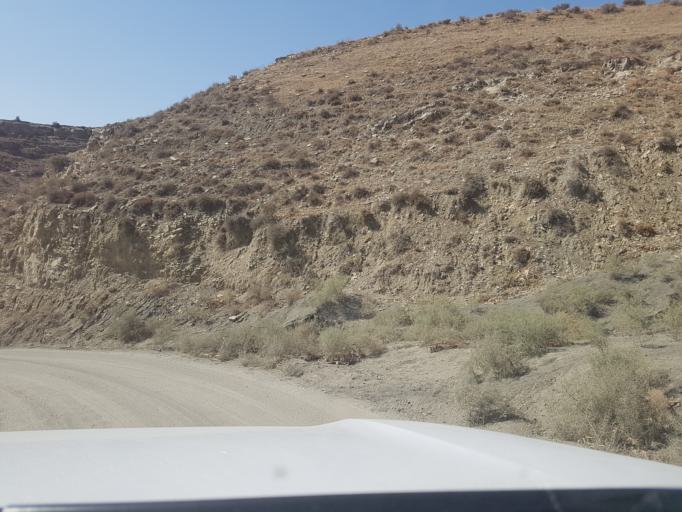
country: TM
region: Ahal
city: Baharly
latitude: 38.2409
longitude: 56.8898
